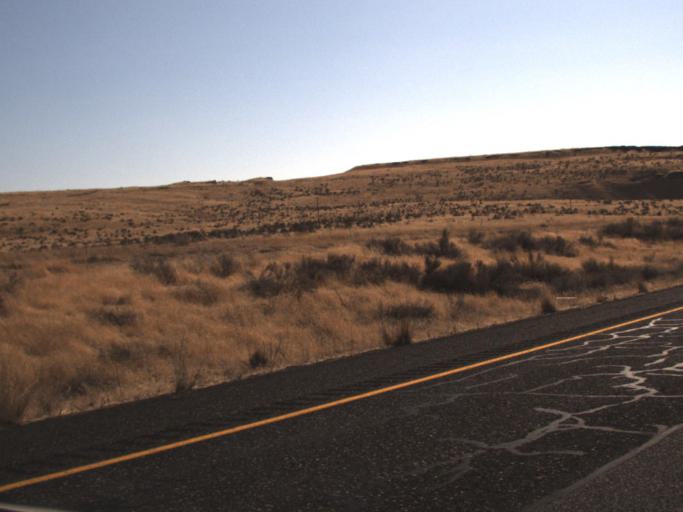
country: US
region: Washington
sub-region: Franklin County
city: Basin City
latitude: 46.4890
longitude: -119.0130
